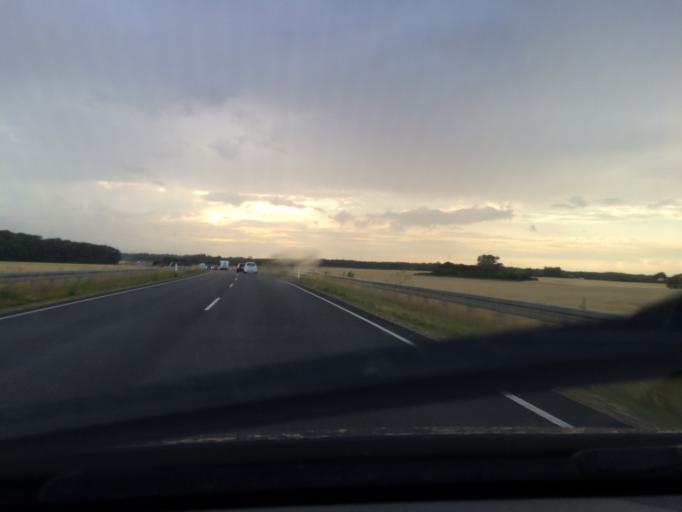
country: DK
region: Zealand
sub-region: Guldborgsund Kommune
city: Nykobing Falster
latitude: 54.7757
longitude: 11.9123
